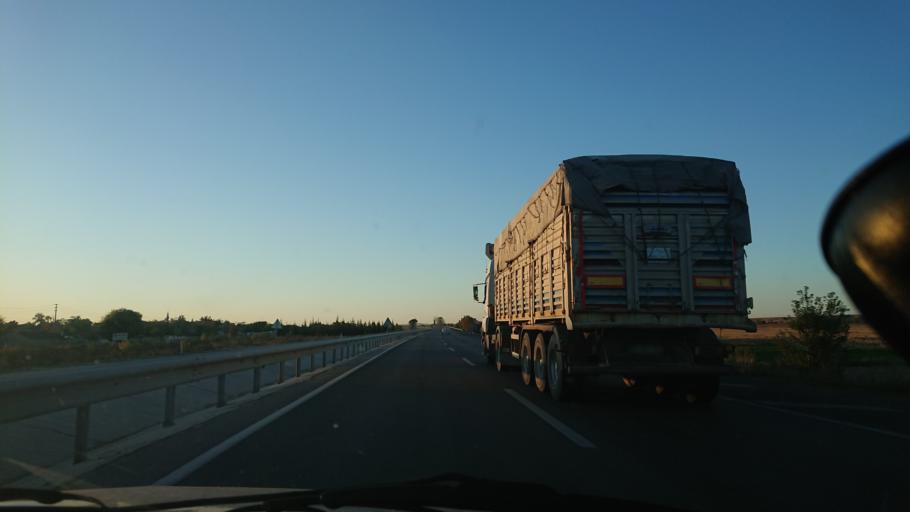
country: TR
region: Eskisehir
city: Mahmudiye
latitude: 39.5327
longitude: 30.9472
